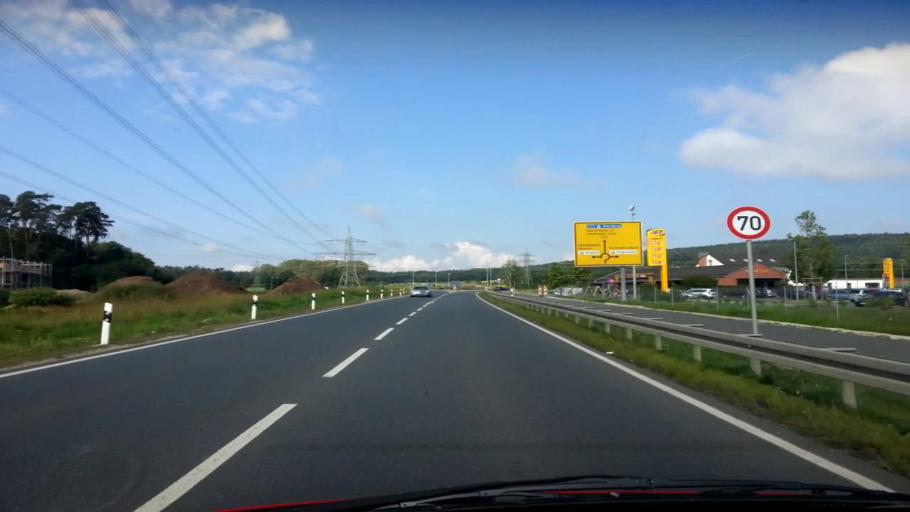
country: DE
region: Bavaria
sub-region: Upper Franconia
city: Hausen
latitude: 49.6951
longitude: 11.0397
